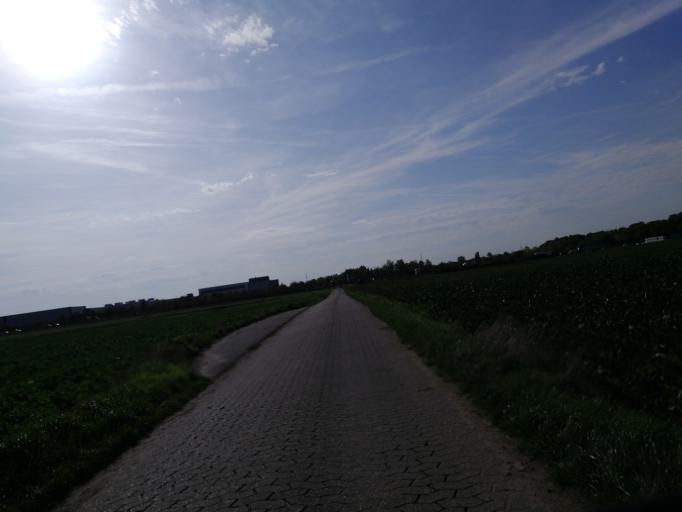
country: DE
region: North Rhine-Westphalia
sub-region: Regierungsbezirk Dusseldorf
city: Dusseldorf
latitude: 51.1633
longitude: 6.7759
